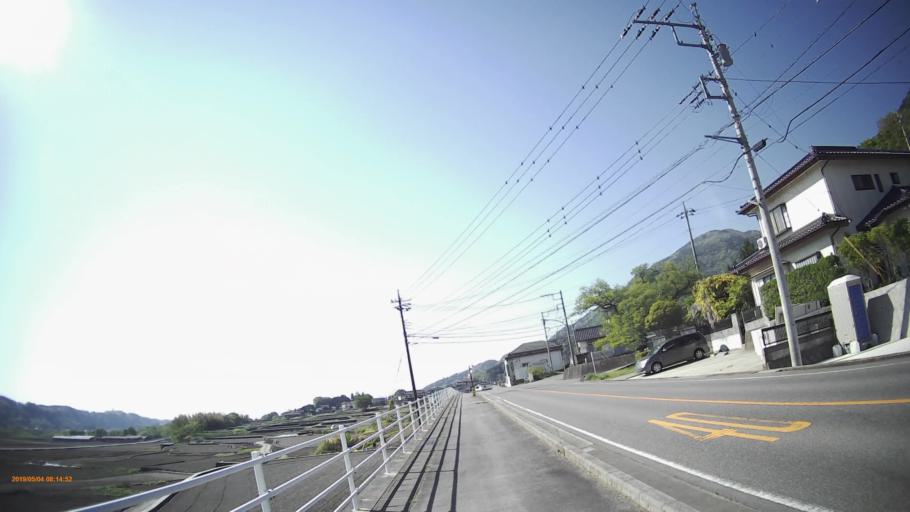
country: JP
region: Yamanashi
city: Nirasaki
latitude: 35.7373
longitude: 138.4088
